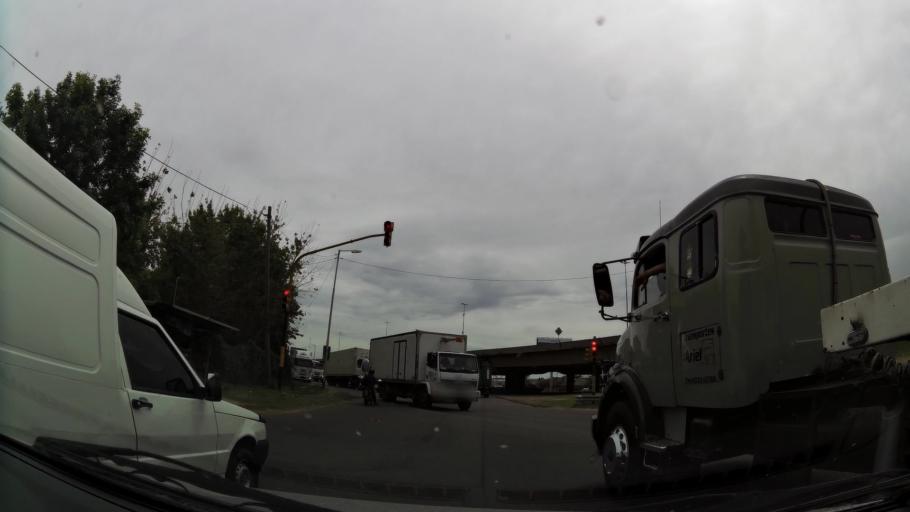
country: AR
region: Buenos Aires
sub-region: Partido de Avellaneda
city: Avellaneda
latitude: -34.6659
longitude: -58.3440
